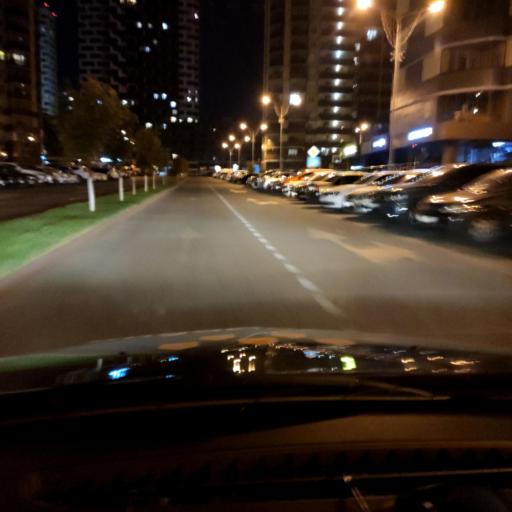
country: RU
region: Voronezj
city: Voronezh
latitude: 51.7151
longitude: 39.1945
